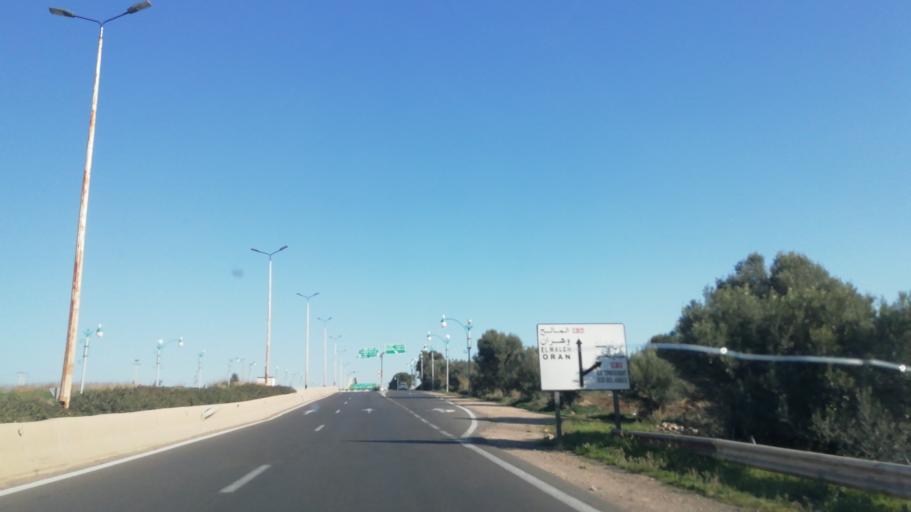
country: DZ
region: Ain Temouchent
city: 'Ain Temouchent
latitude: 35.2999
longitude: -1.1666
